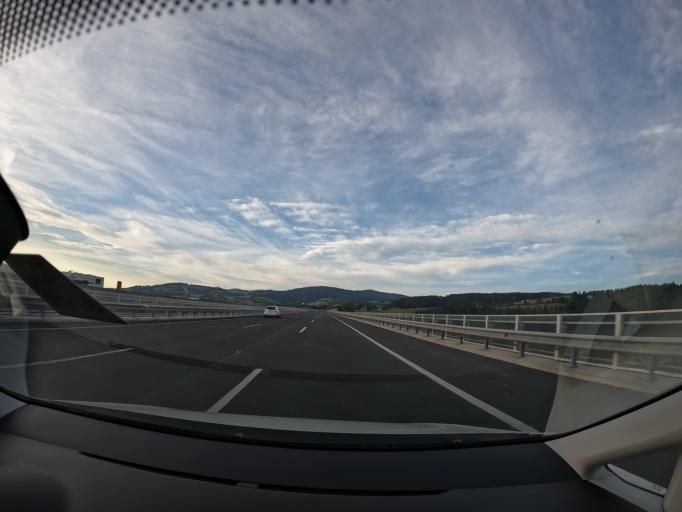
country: AT
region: Carinthia
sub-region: Politischer Bezirk Wolfsberg
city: Bad Sankt Leonhard im Lavanttal
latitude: 46.9246
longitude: 14.8237
